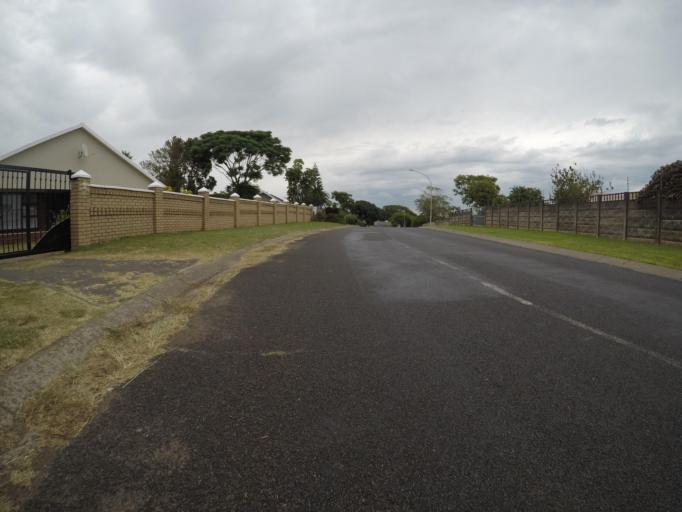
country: ZA
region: Eastern Cape
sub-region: Buffalo City Metropolitan Municipality
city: East London
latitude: -32.9939
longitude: 27.8504
